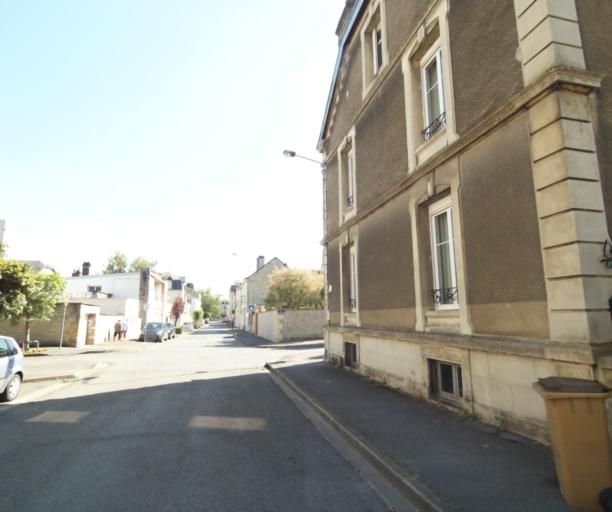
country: FR
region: Champagne-Ardenne
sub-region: Departement des Ardennes
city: Charleville-Mezieres
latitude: 49.7643
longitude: 4.7212
